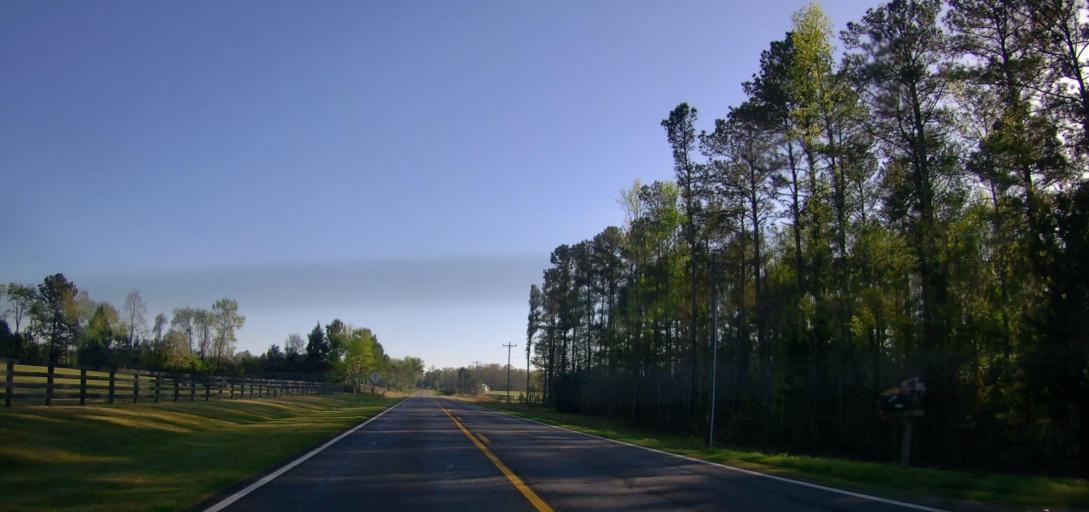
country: US
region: Georgia
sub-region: Butts County
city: Indian Springs
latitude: 33.1862
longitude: -83.9577
